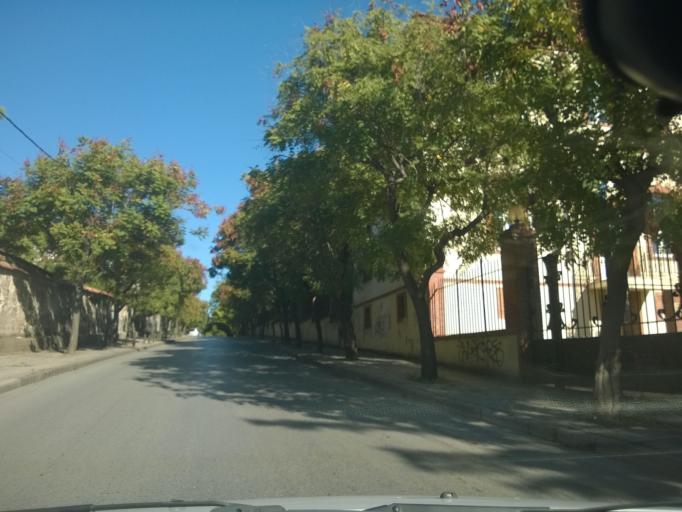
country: GR
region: Central Macedonia
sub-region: Nomos Thessalonikis
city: Kalamaria
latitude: 40.5933
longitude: 22.9543
